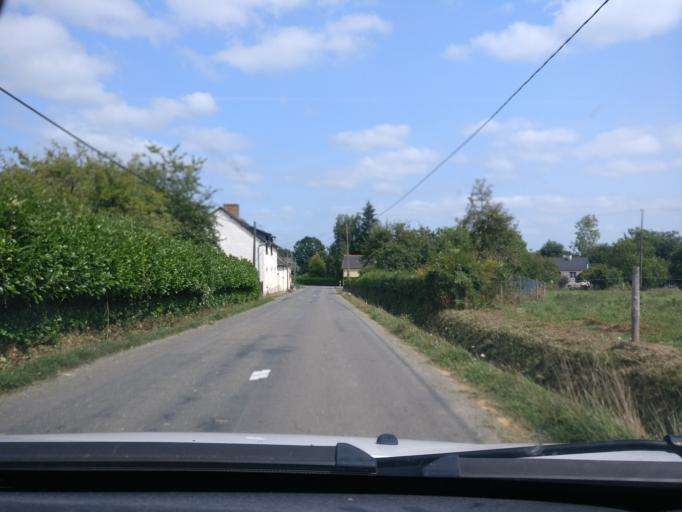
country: FR
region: Brittany
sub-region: Departement d'Ille-et-Vilaine
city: Chasne-sur-Illet
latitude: 48.2369
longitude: -1.5738
